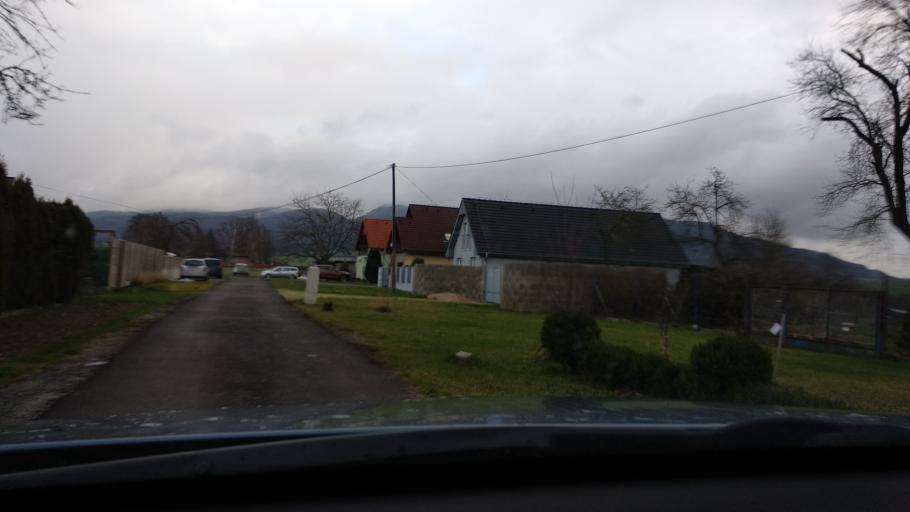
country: SK
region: Trenciansky
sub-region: Okres Trencin
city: Trencin
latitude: 48.8479
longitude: 18.0449
